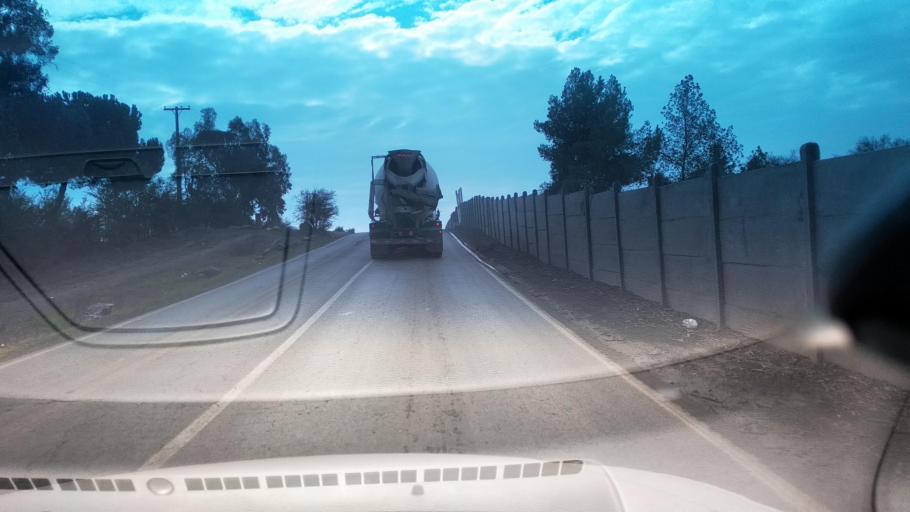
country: CL
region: Santiago Metropolitan
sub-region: Provincia de Santiago
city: Lo Prado
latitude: -33.4483
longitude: -70.7996
